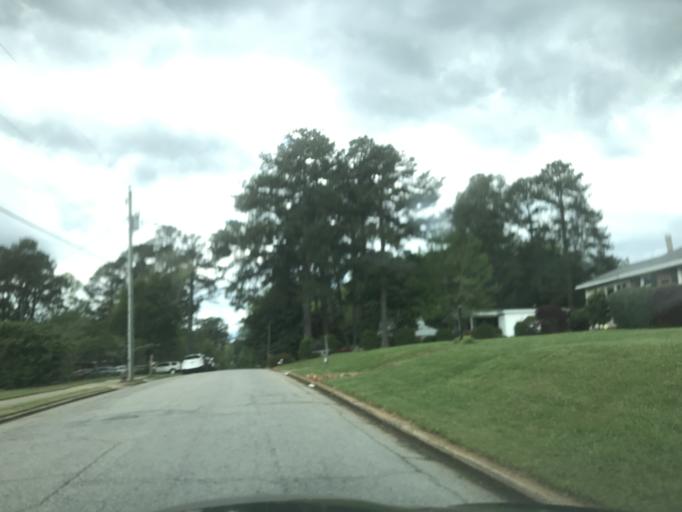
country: US
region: North Carolina
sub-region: Wake County
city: West Raleigh
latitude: 35.7776
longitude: -78.7112
